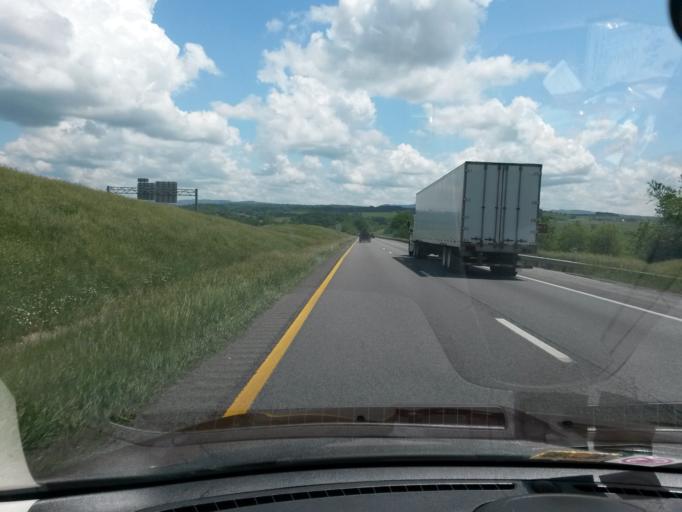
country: US
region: Virginia
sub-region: Wythe County
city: Wytheville
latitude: 36.9377
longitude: -80.9156
